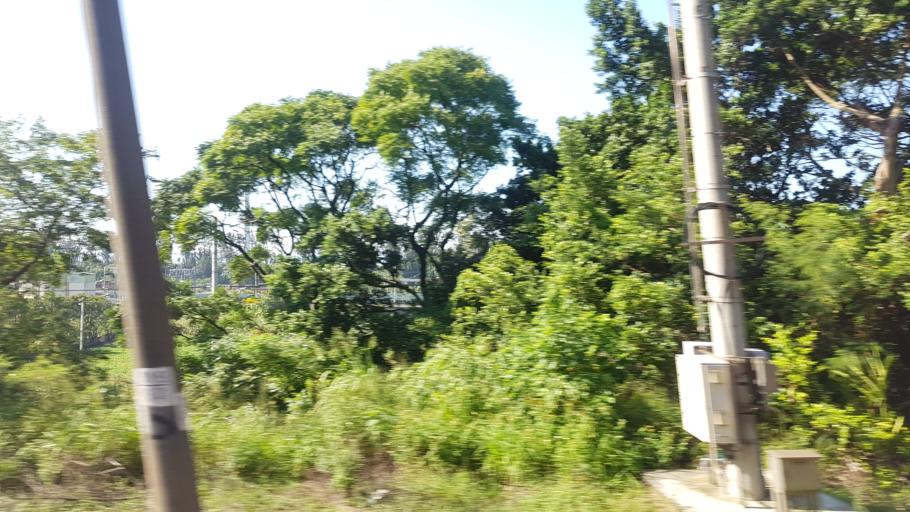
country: TW
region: Taiwan
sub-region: Hsinchu
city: Hsinchu
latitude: 24.7330
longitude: 120.8836
